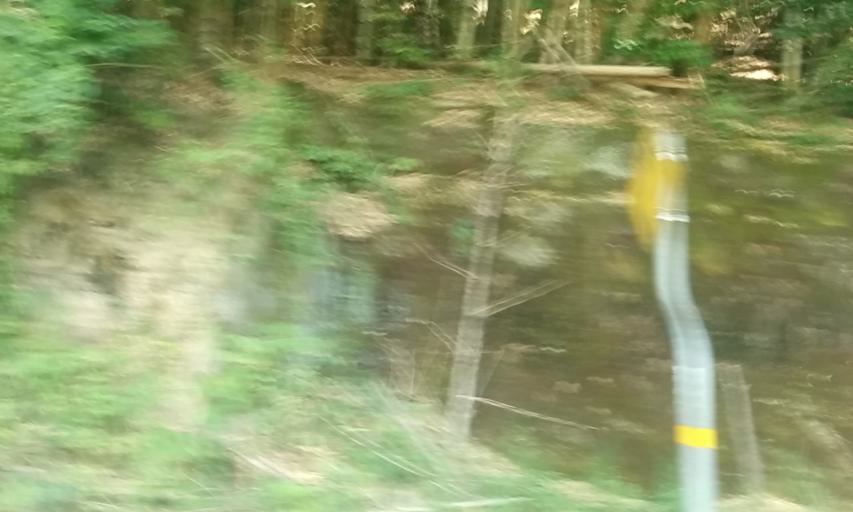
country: JP
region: Kyoto
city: Ayabe
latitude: 35.2018
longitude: 135.1945
